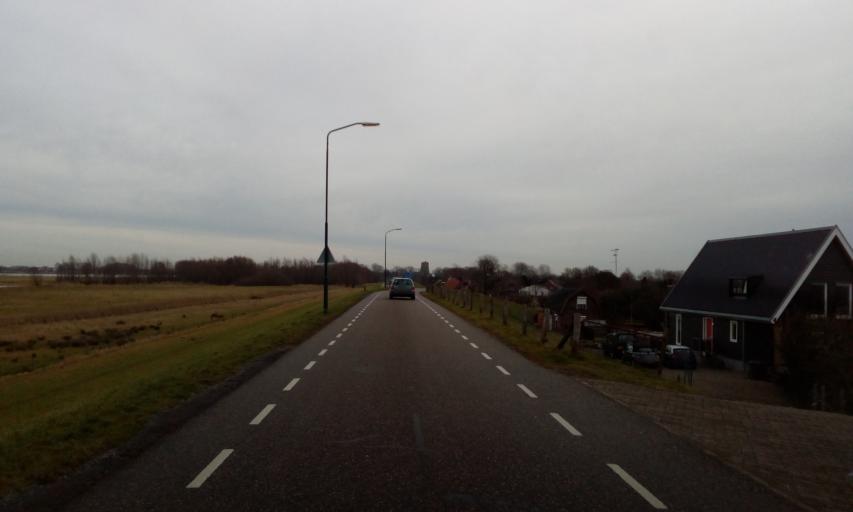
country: NL
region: North Brabant
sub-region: Gemeente Woudrichem
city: Woudrichem
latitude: 51.8162
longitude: 4.9844
